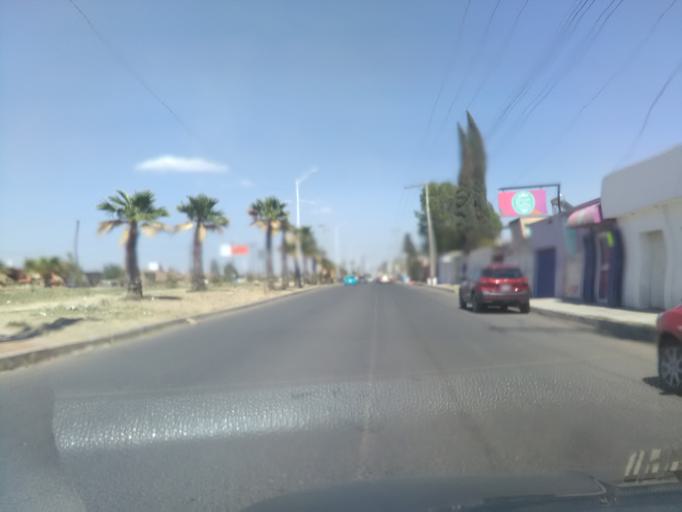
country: MX
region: Durango
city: Victoria de Durango
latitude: 24.0468
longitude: -104.6420
